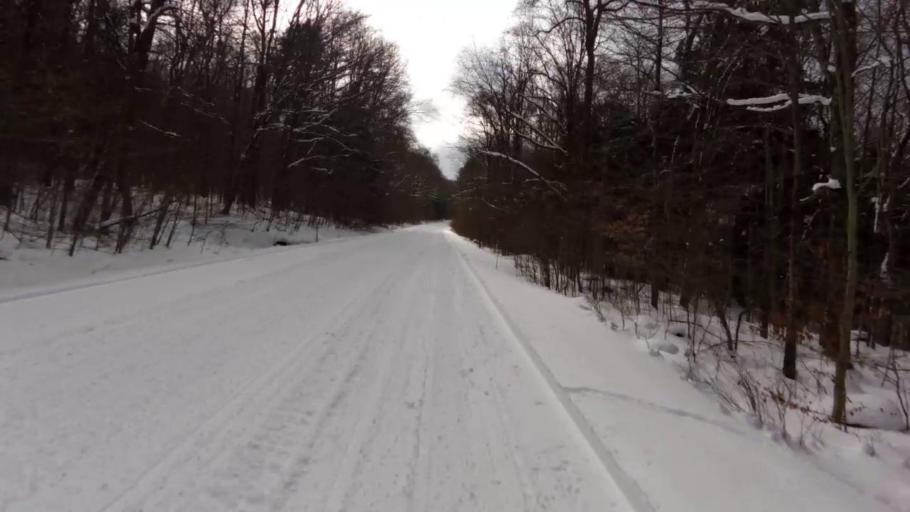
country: US
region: New York
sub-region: Cattaraugus County
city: Salamanca
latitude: 42.0829
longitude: -78.7484
